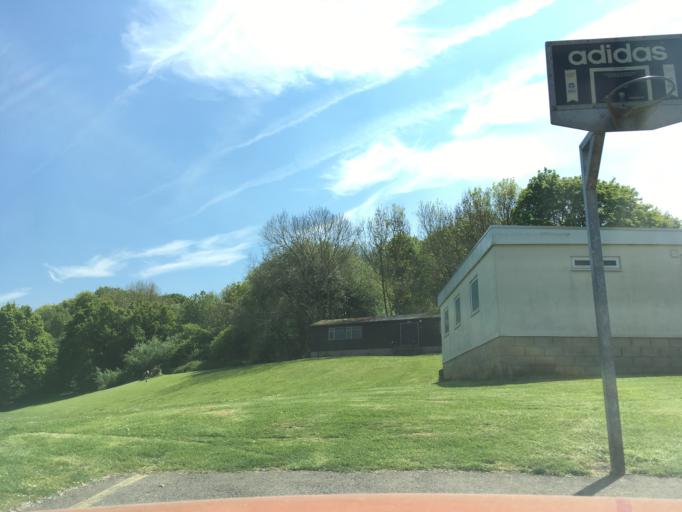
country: GB
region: England
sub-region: Gloucestershire
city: Nailsworth
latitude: 51.6930
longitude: -2.2151
